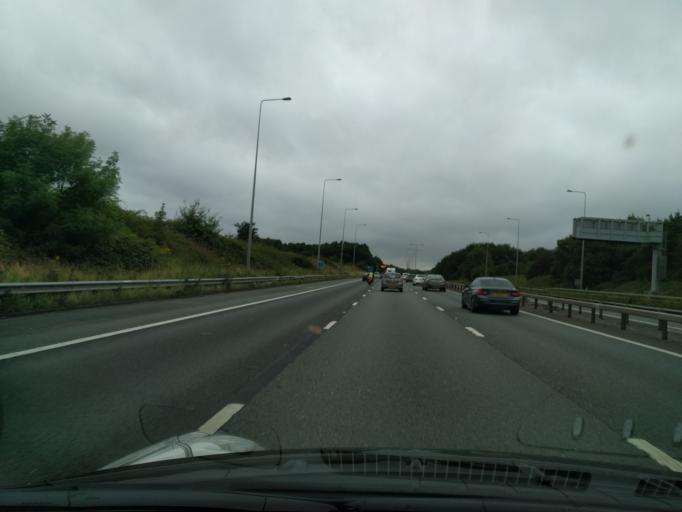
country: GB
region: England
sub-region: St. Helens
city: Newton-le-Willows
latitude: 53.4608
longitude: -2.6127
